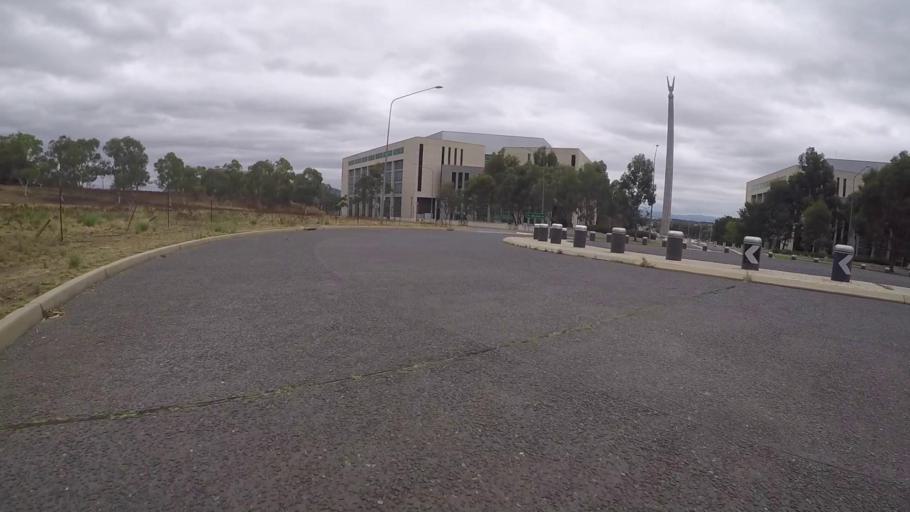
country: AU
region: Australian Capital Territory
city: Canberra
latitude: -35.2970
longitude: 149.1539
